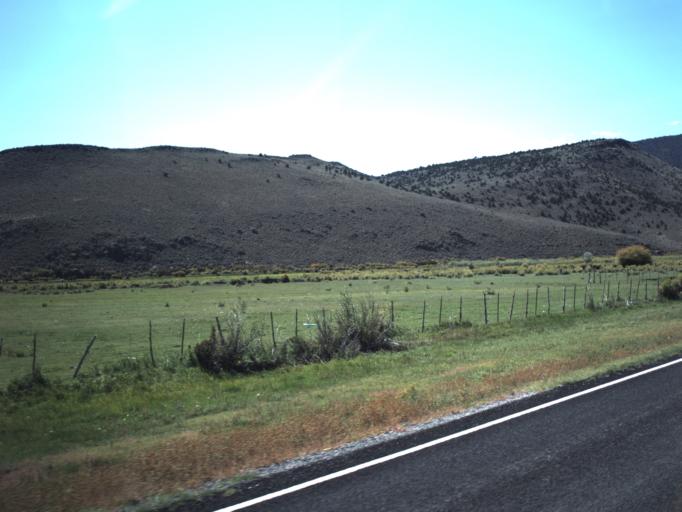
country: US
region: Utah
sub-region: Piute County
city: Junction
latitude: 38.1665
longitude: -112.0255
